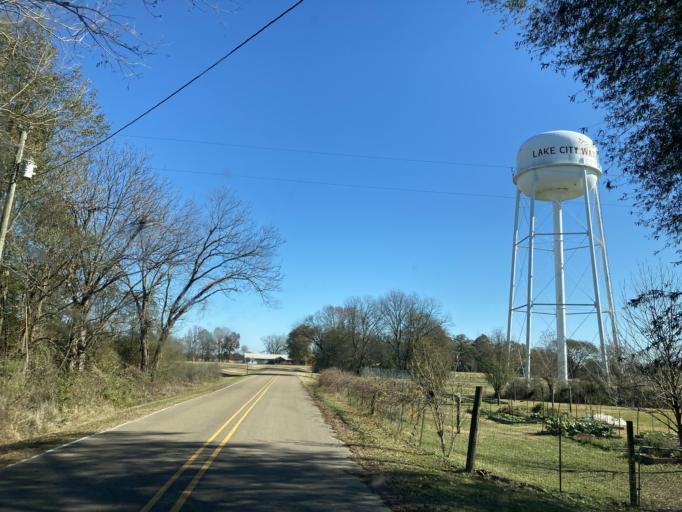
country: US
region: Mississippi
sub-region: Yazoo County
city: Yazoo City
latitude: 32.9232
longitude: -90.4935
